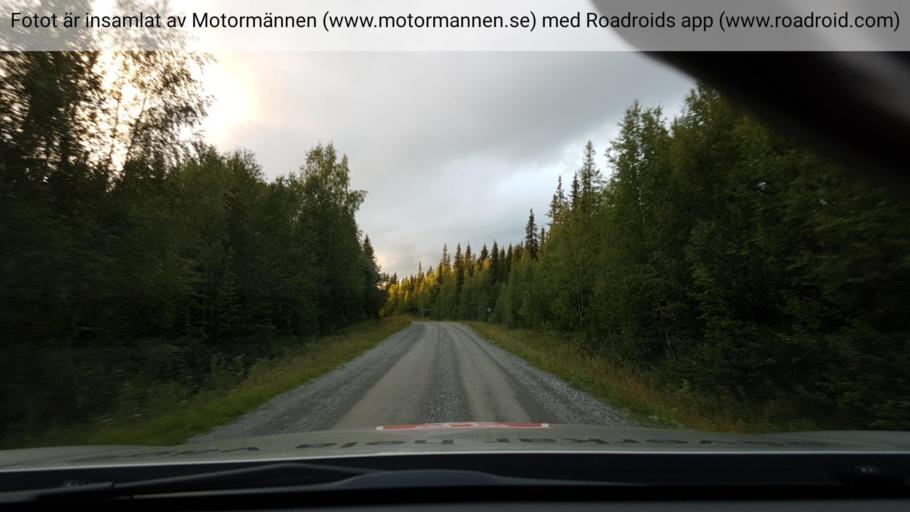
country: SE
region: Vaesterbotten
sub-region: Vilhelmina Kommun
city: Sjoberg
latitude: 65.5533
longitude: 15.4111
